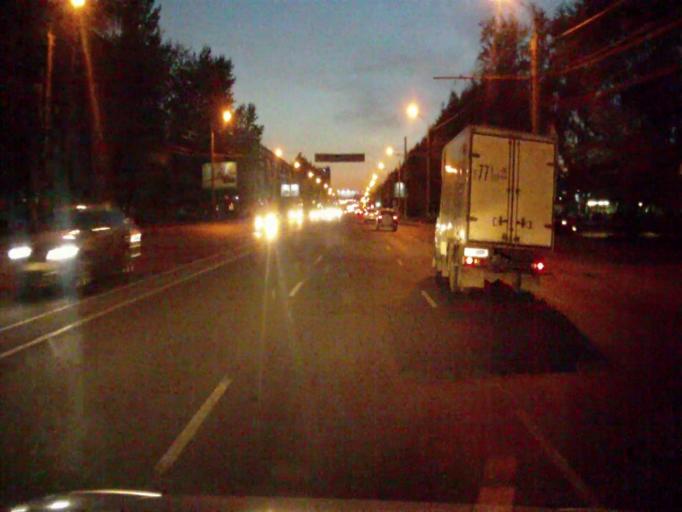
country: RU
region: Chelyabinsk
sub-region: Gorod Chelyabinsk
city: Chelyabinsk
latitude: 55.1786
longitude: 61.3448
